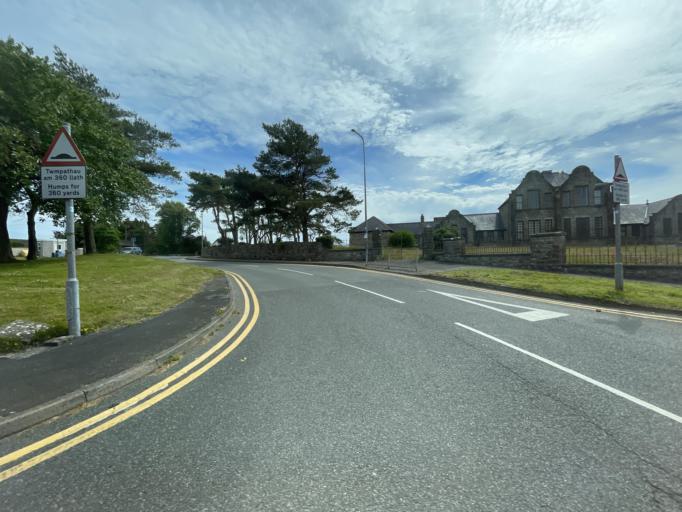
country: GB
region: Wales
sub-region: Anglesey
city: Llangefni
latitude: 53.2570
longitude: -4.3168
